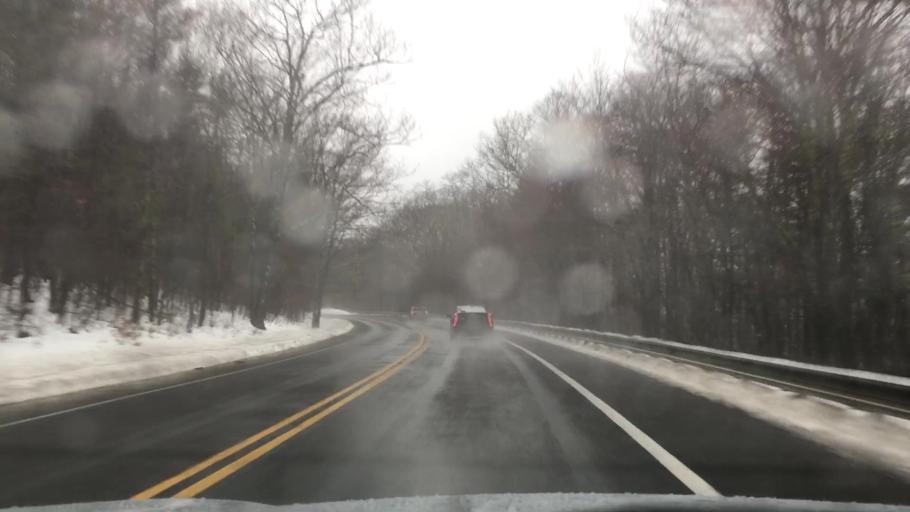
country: US
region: Massachusetts
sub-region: Franklin County
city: Shutesbury
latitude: 42.4423
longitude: -72.3876
